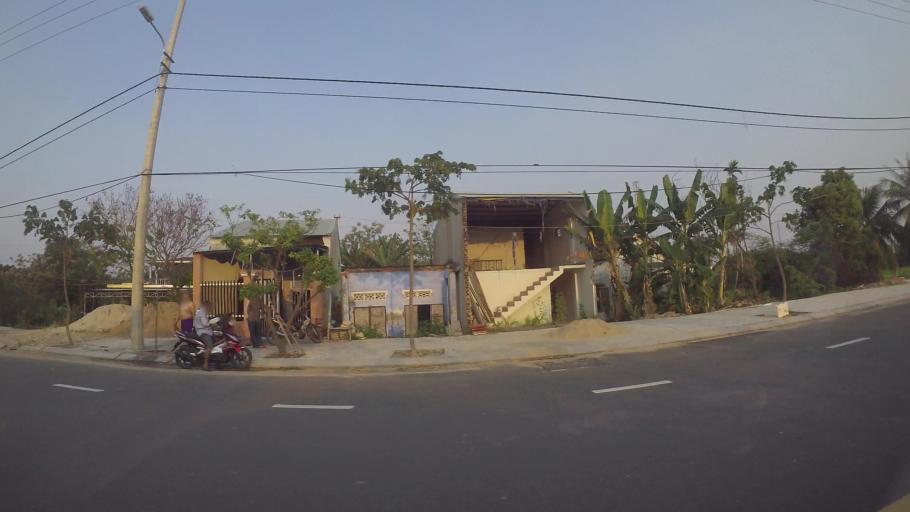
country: VN
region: Da Nang
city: Ngu Hanh Son
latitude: 15.9667
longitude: 108.2314
